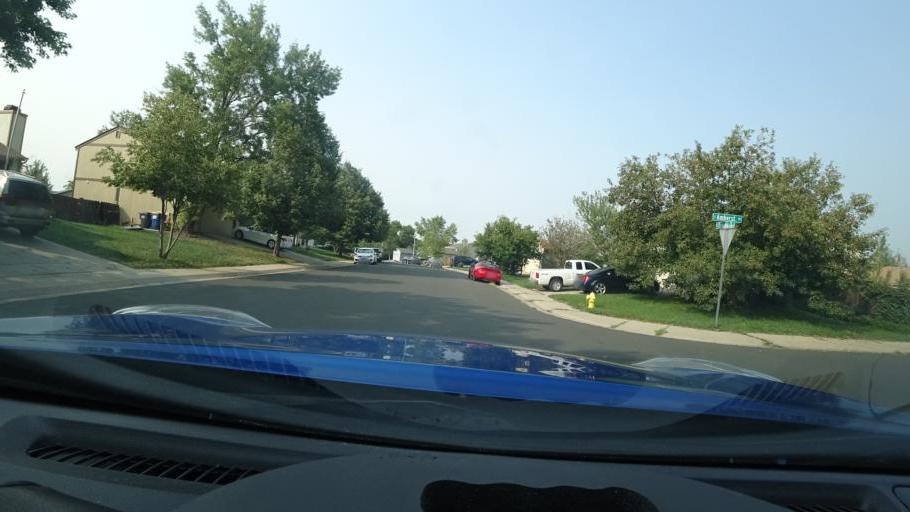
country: US
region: Colorado
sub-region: Adams County
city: Aurora
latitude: 39.6654
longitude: -104.7828
